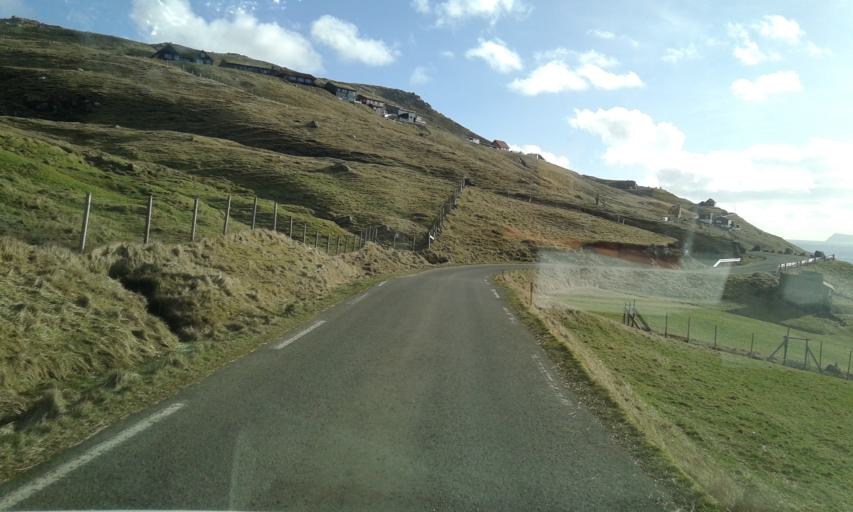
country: FO
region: Streymoy
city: Argir
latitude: 61.9882
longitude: -6.8683
